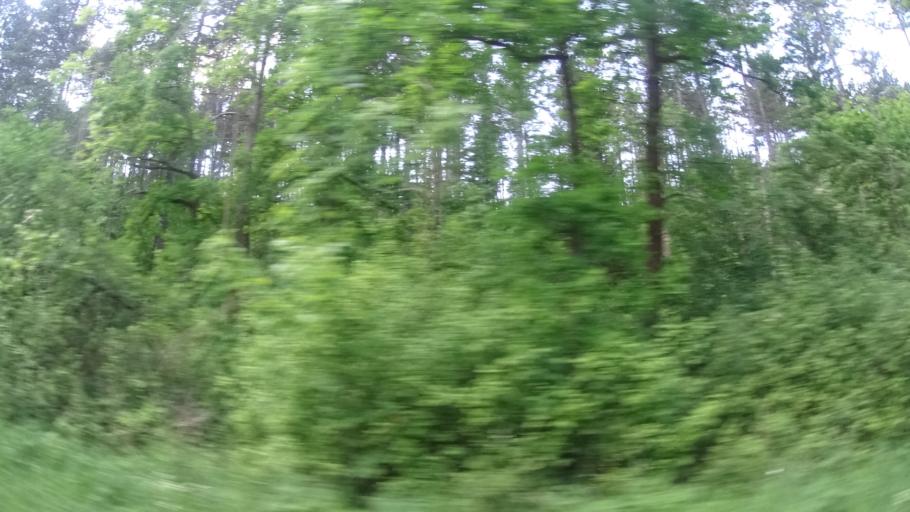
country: DE
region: Thuringia
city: Plaue
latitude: 50.8215
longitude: 10.9077
